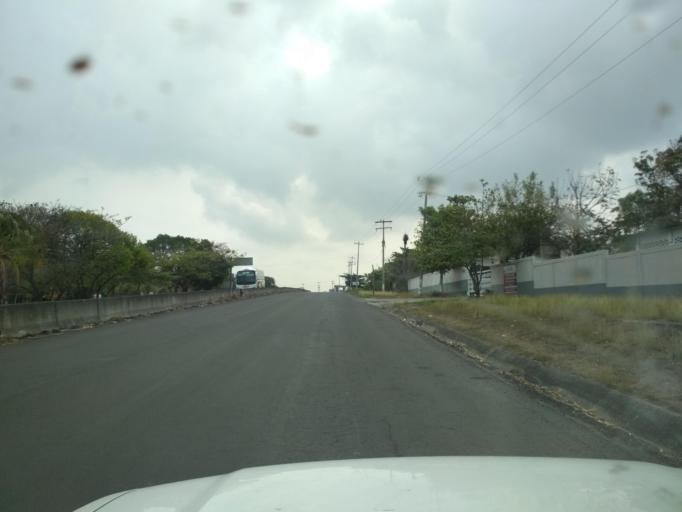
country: MX
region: Veracruz
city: Paso del Toro
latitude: 19.0178
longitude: -96.1380
